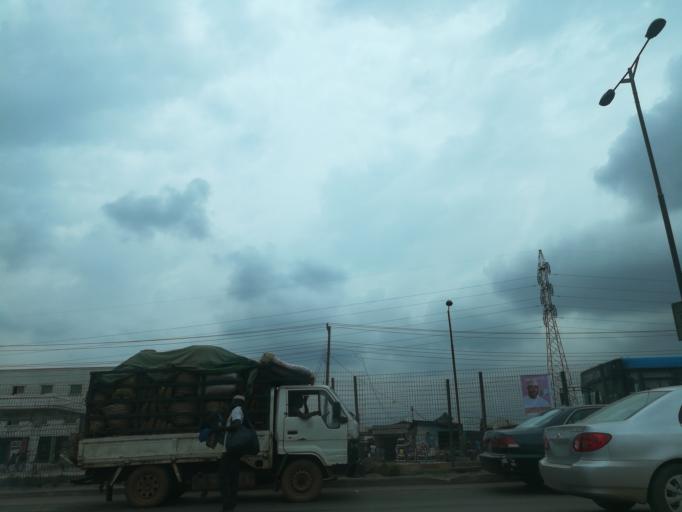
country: NG
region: Lagos
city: Ojota
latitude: 6.6035
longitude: 3.3904
